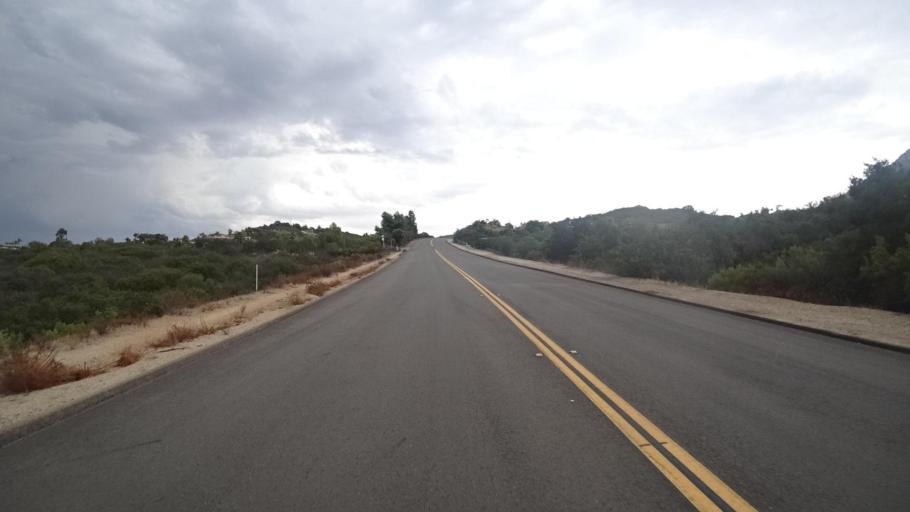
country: US
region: California
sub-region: San Diego County
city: San Pasqual
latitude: 33.0247
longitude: -116.9561
